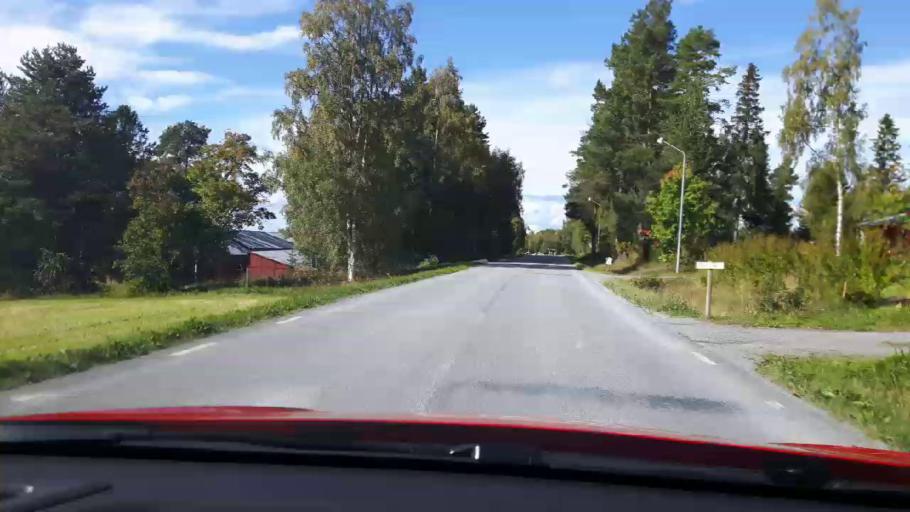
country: SE
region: Jaemtland
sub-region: OEstersunds Kommun
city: Ostersund
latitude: 63.0369
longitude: 14.4671
